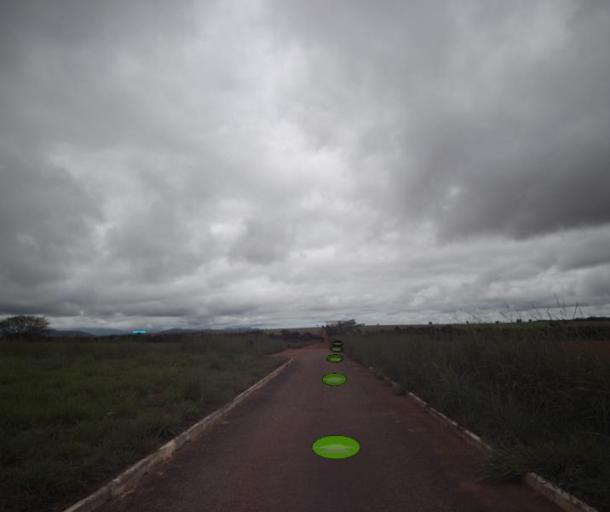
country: BR
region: Goias
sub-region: Barro Alto
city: Barro Alto
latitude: -14.8377
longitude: -49.0319
